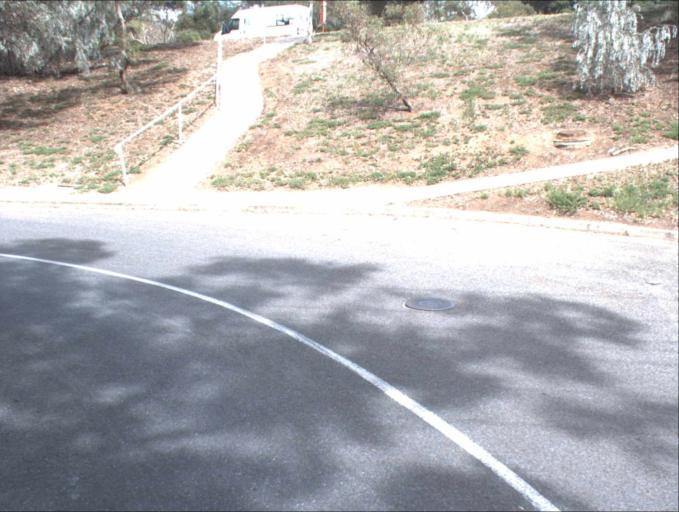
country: AU
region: South Australia
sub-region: Campbelltown
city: Paradise
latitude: -34.8639
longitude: 138.6620
